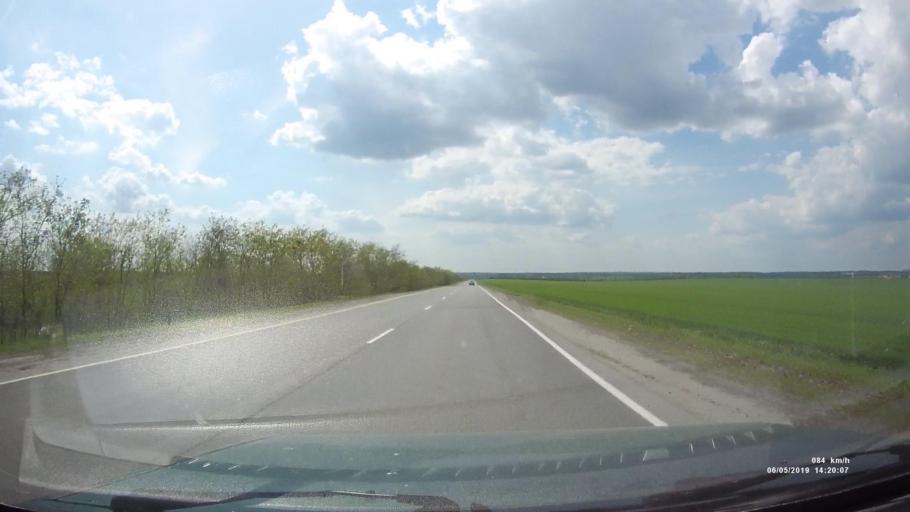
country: RU
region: Rostov
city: Kamenolomni
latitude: 47.6324
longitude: 40.2194
